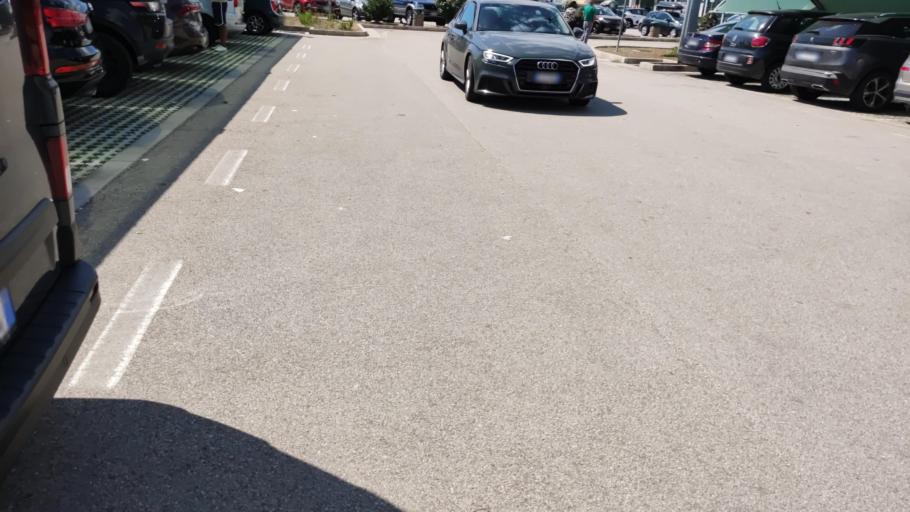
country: IT
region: Campania
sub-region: Provincia di Salerno
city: Serre
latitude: 40.6182
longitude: 15.1662
